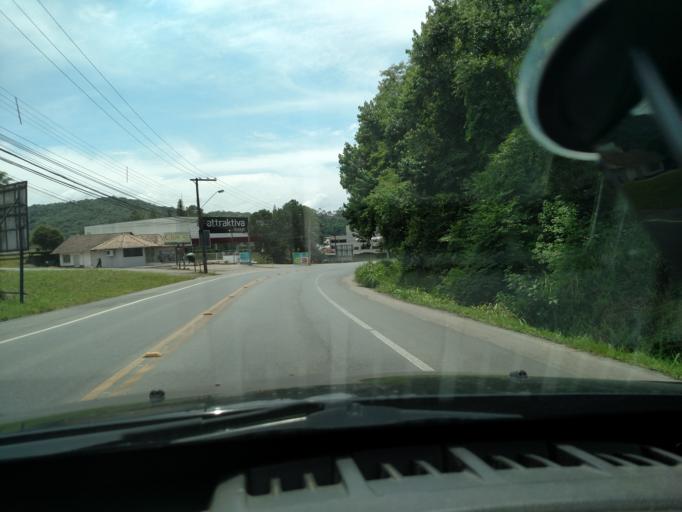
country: BR
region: Santa Catarina
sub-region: Blumenau
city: Blumenau
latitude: -26.9064
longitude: -49.0397
